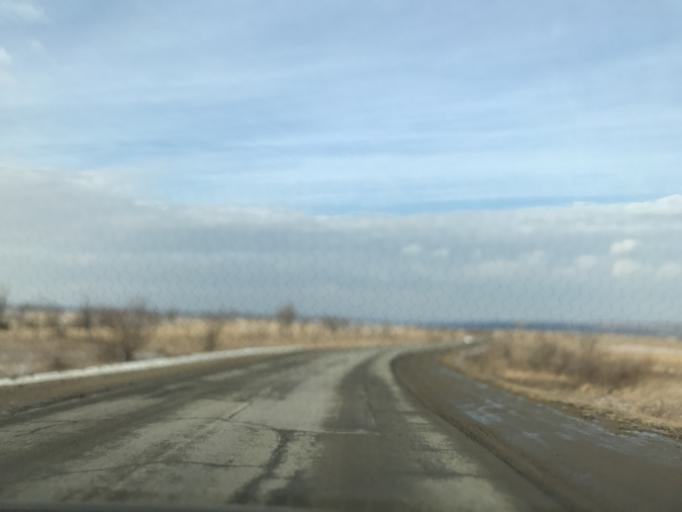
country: RU
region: Rostov
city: Staraya Stanitsa
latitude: 48.2714
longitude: 40.3491
